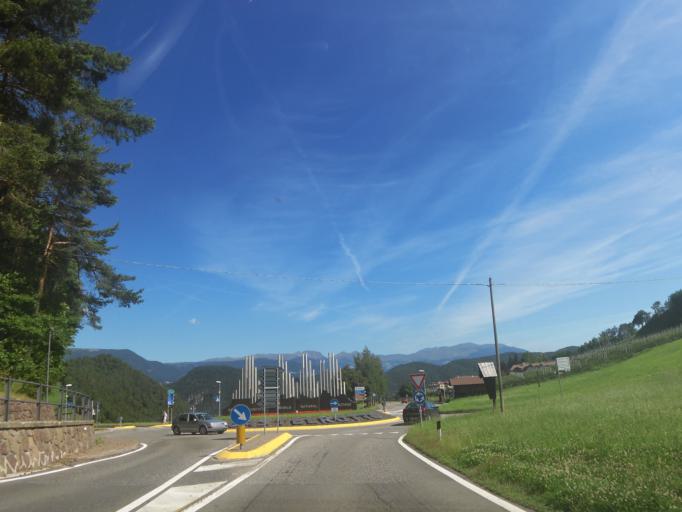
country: IT
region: Trentino-Alto Adige
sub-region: Bolzano
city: Castelrotto
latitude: 46.5564
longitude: 11.5565
